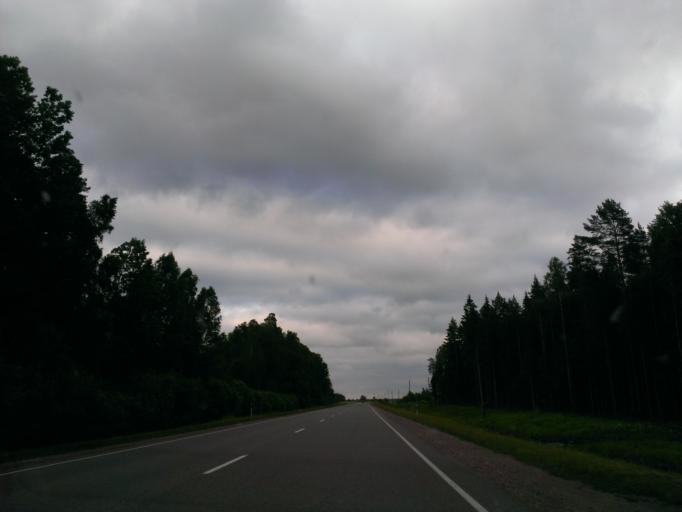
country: LV
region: Saldus Rajons
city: Saldus
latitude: 56.6718
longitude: 22.2822
